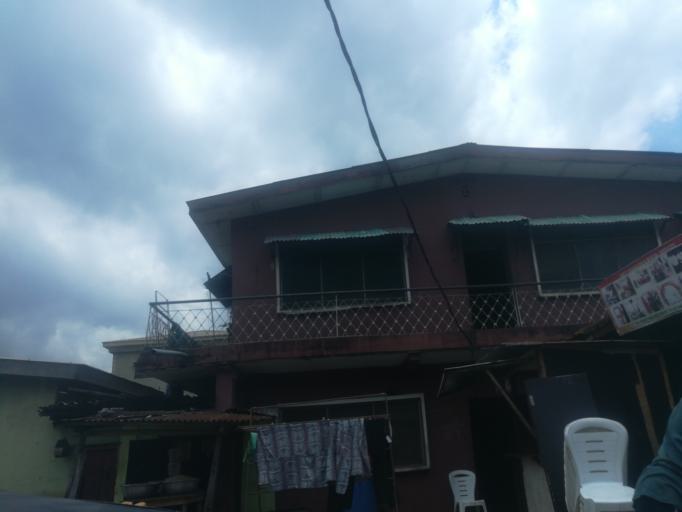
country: NG
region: Lagos
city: Somolu
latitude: 6.5524
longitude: 3.3927
